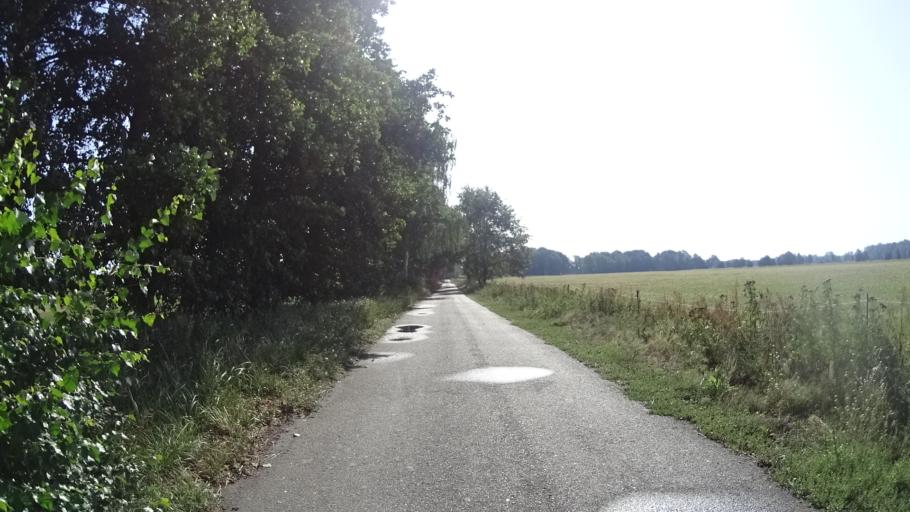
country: DE
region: Brandenburg
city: Straupitz
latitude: 51.8981
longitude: 14.1021
